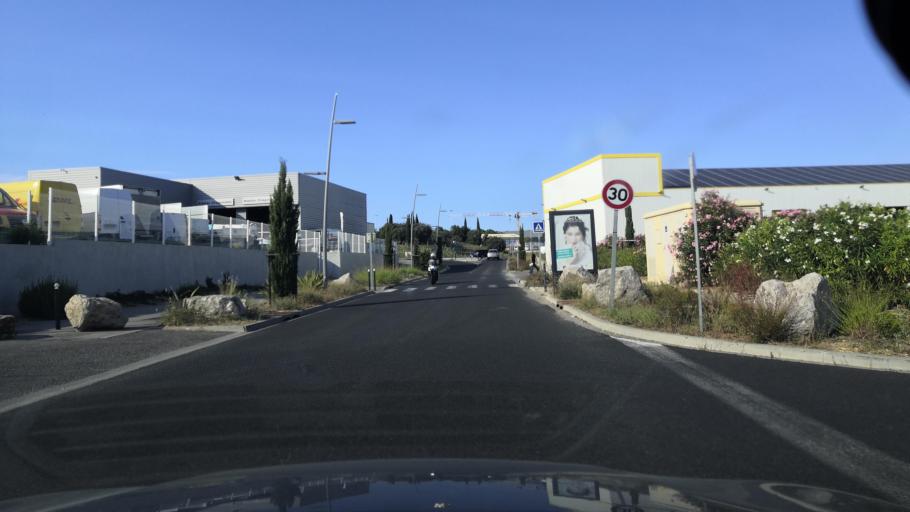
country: FR
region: Languedoc-Roussillon
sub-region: Departement de l'Herault
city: Lattes
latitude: 43.5738
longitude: 3.8672
